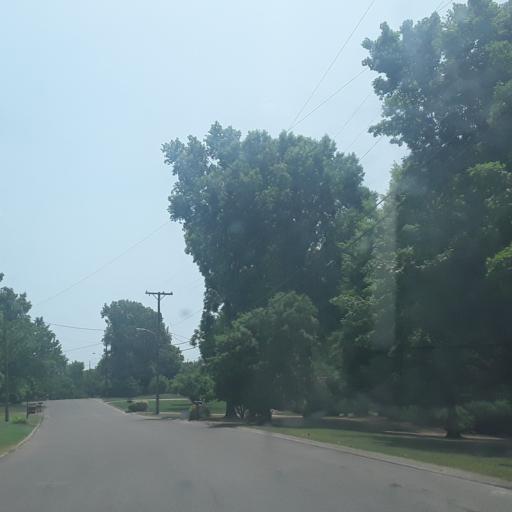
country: US
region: Tennessee
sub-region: Williamson County
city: Brentwood
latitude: 36.0582
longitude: -86.7584
